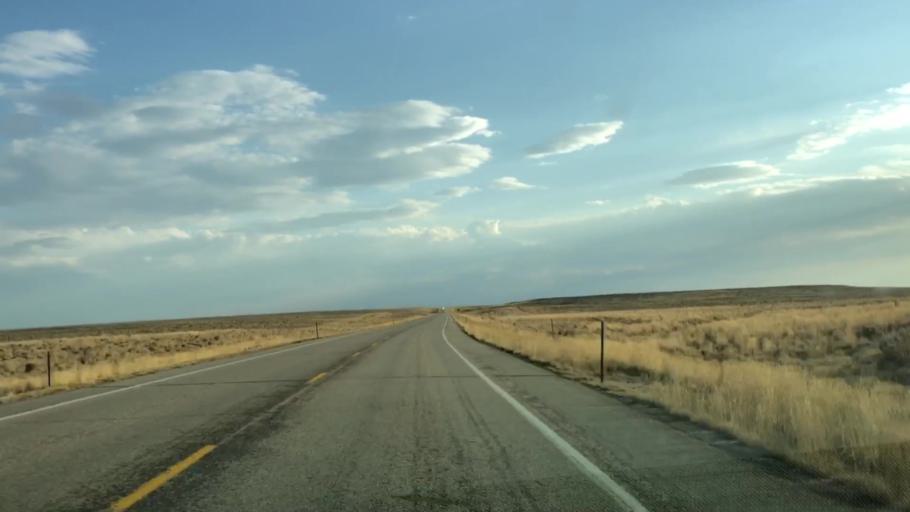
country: US
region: Wyoming
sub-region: Sweetwater County
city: North Rock Springs
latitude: 42.2148
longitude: -109.4707
